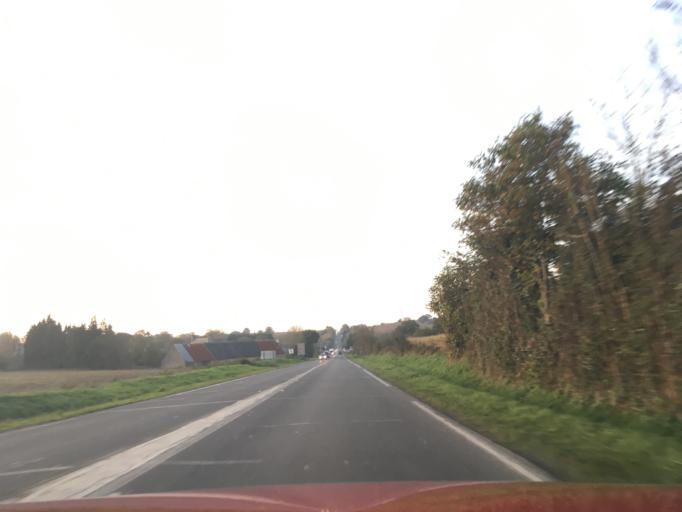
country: FR
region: Lower Normandy
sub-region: Departement de la Manche
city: Saint-Planchers
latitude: 48.7865
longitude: -1.5044
